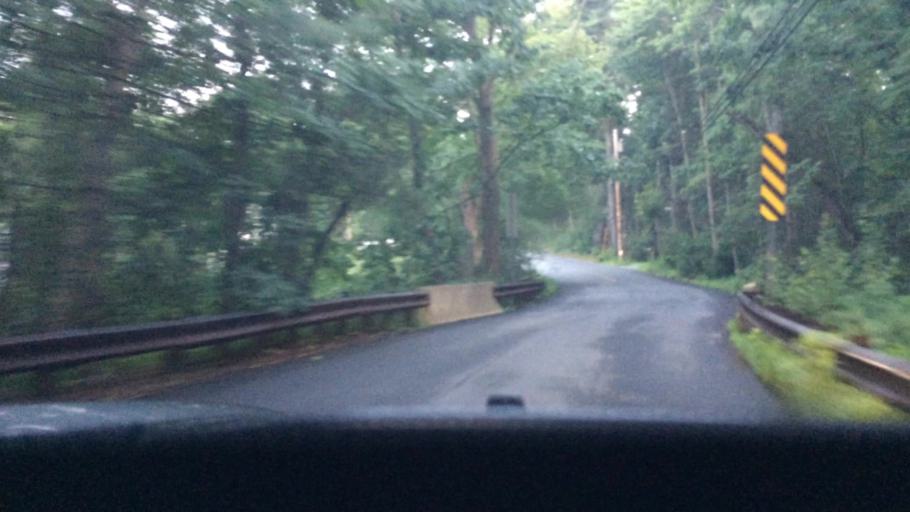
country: US
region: Massachusetts
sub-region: Middlesex County
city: North Reading
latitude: 42.6116
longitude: -71.0987
